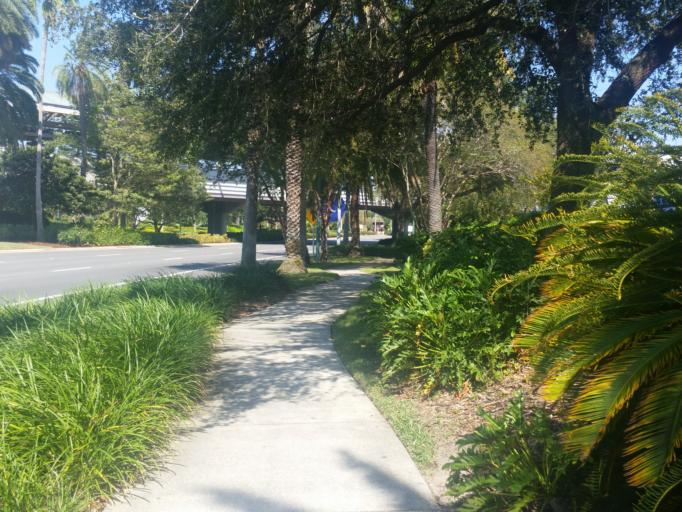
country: US
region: Florida
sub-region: Orange County
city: Tangelo Park
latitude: 28.4731
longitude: -81.4640
